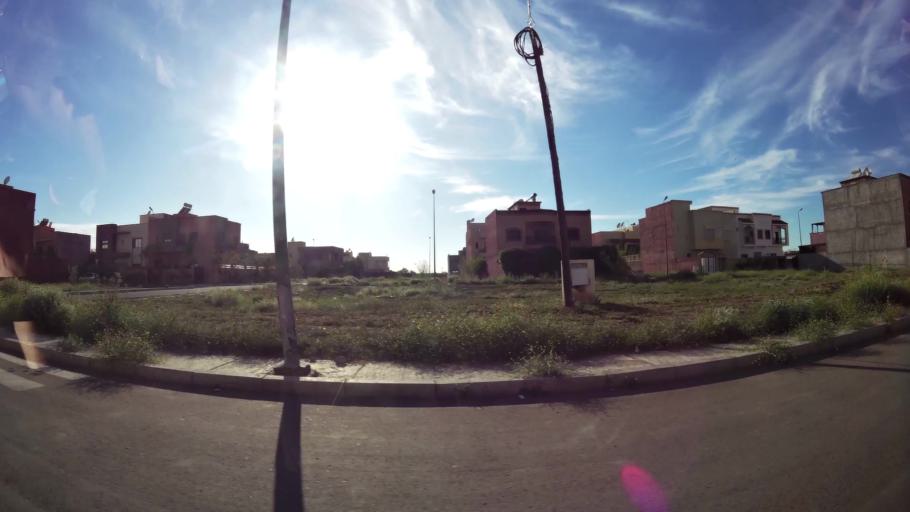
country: MA
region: Marrakech-Tensift-Al Haouz
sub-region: Marrakech
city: Marrakesh
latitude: 31.6798
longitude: -8.0625
